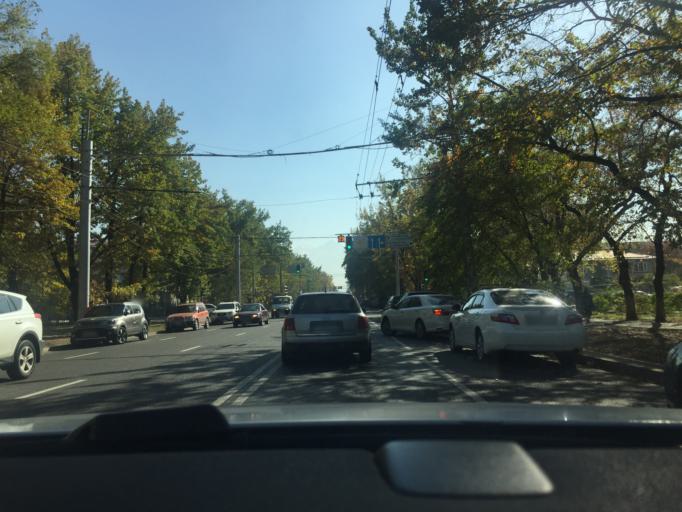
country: KZ
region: Almaty Qalasy
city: Almaty
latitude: 43.2509
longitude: 76.9025
